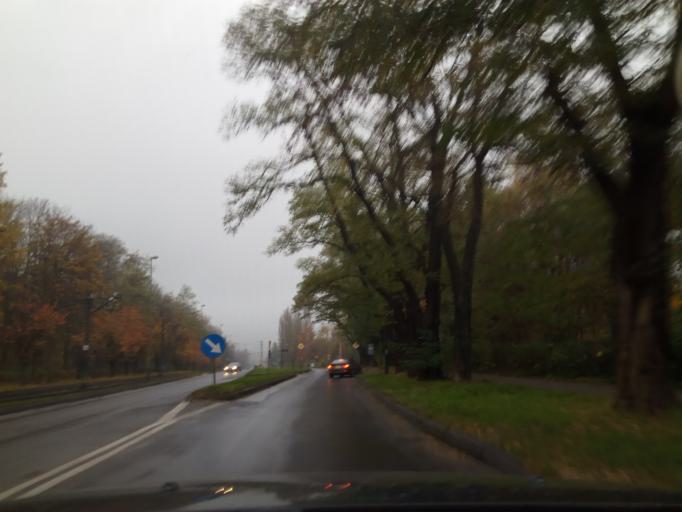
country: PL
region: Lesser Poland Voivodeship
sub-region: Powiat wielicki
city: Kokotow
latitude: 50.0801
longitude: 20.0660
